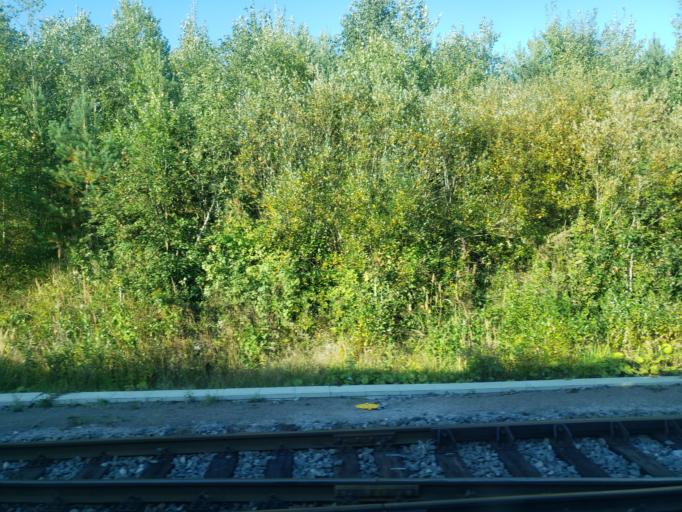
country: FI
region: South Karelia
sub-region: Lappeenranta
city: Lappeenranta
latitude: 60.8679
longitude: 28.2881
